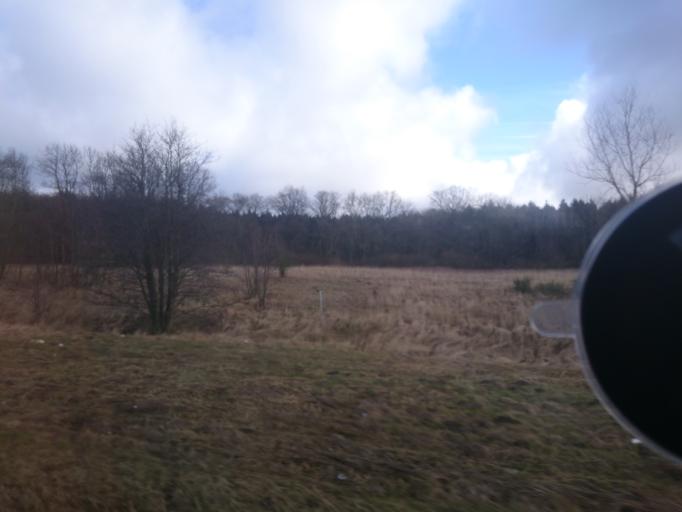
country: DE
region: Mecklenburg-Vorpommern
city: Kavelstorf
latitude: 54.0230
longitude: 12.2012
